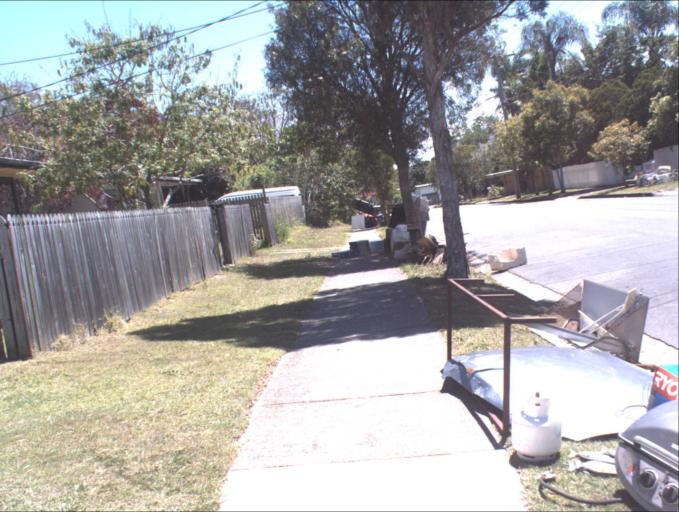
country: AU
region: Queensland
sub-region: Logan
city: Logan City
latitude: -27.6448
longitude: 153.1249
